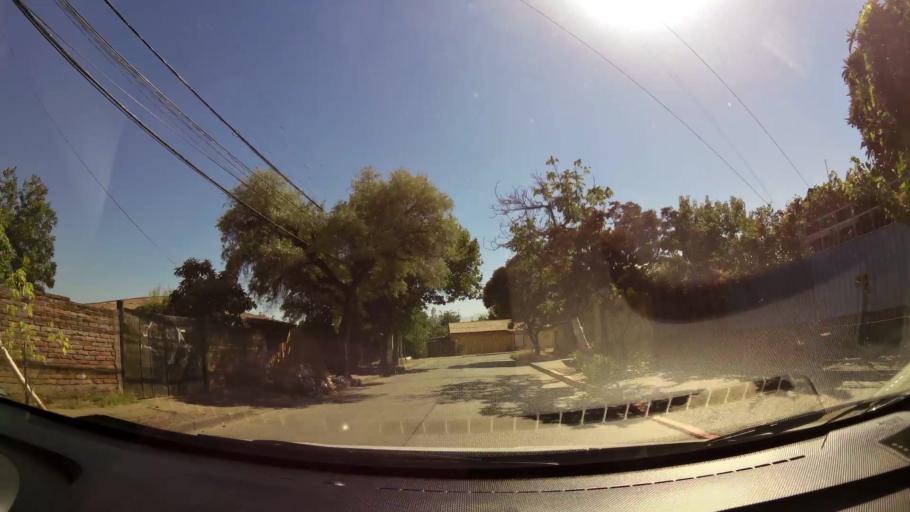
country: CL
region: O'Higgins
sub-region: Provincia de Cachapoal
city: Rancagua
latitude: -34.1738
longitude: -70.7050
